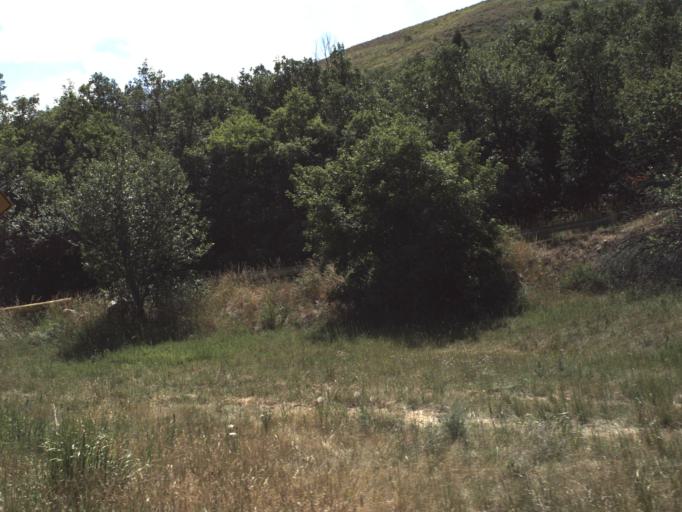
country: US
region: Utah
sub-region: Weber County
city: Wolf Creek
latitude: 41.3299
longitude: -111.6135
